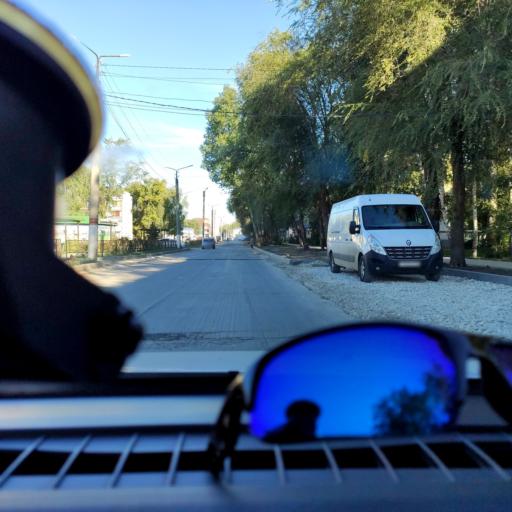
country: RU
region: Samara
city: Chapayevsk
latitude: 52.9525
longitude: 49.6938
